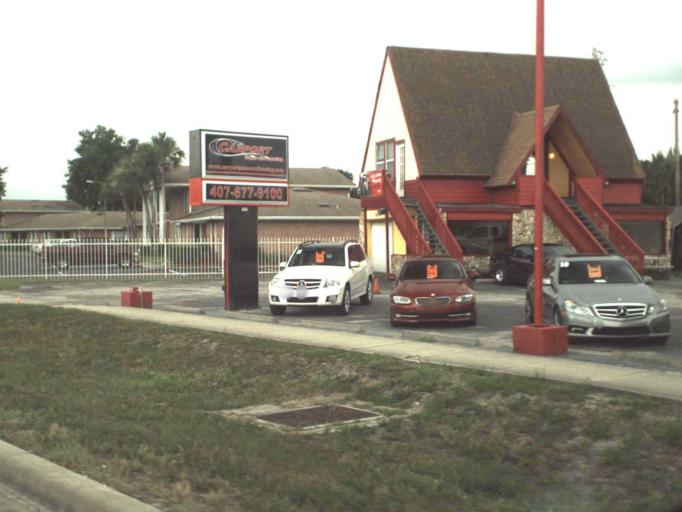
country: US
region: Florida
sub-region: Seminole County
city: Goldenrod
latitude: 28.6220
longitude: -81.3144
